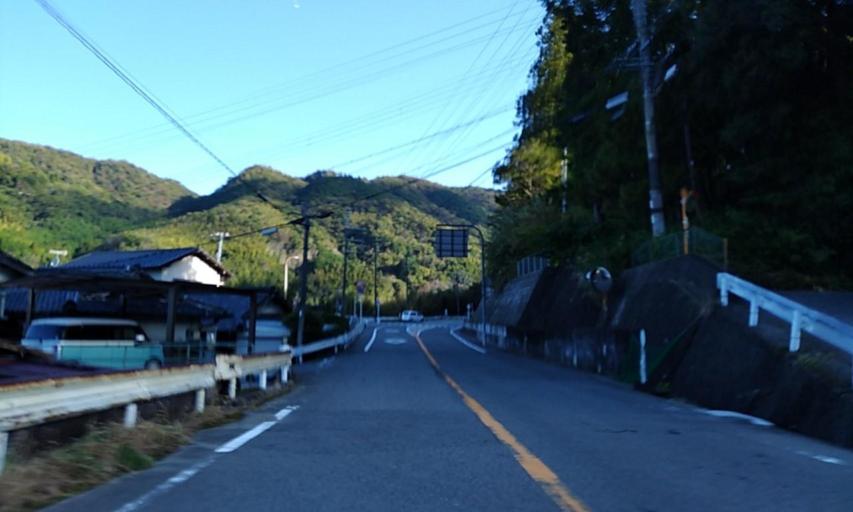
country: JP
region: Wakayama
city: Iwade
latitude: 34.1544
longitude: 135.3194
